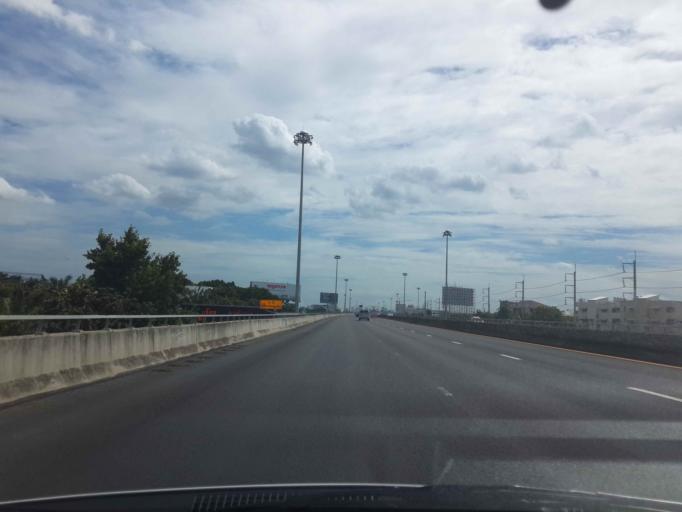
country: TH
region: Bangkok
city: Lat Phrao
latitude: 13.8213
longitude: 100.6266
